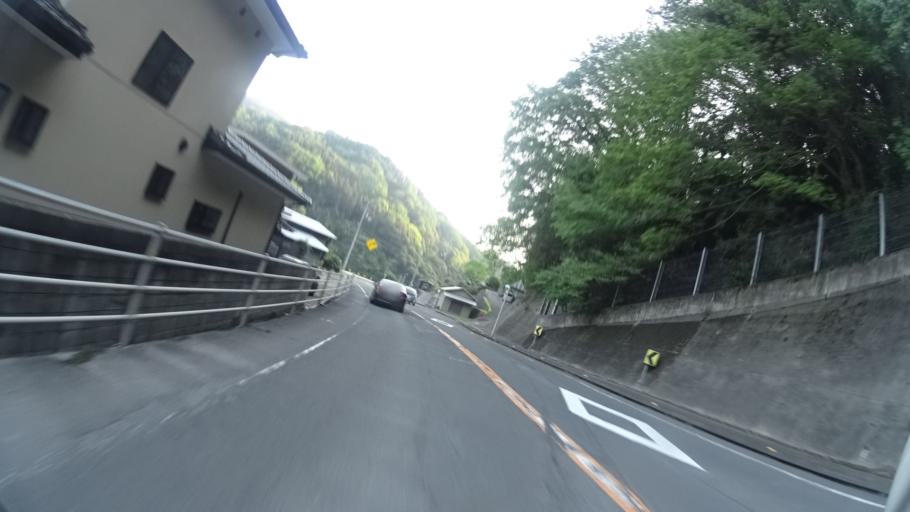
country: JP
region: Ehime
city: Kawanoecho
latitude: 33.9961
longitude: 133.6525
